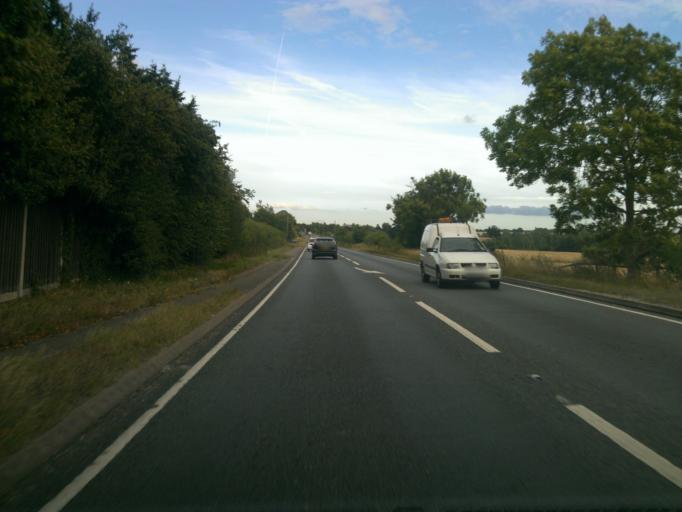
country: GB
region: England
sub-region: Essex
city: Coggeshall
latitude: 51.8721
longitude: 0.6539
